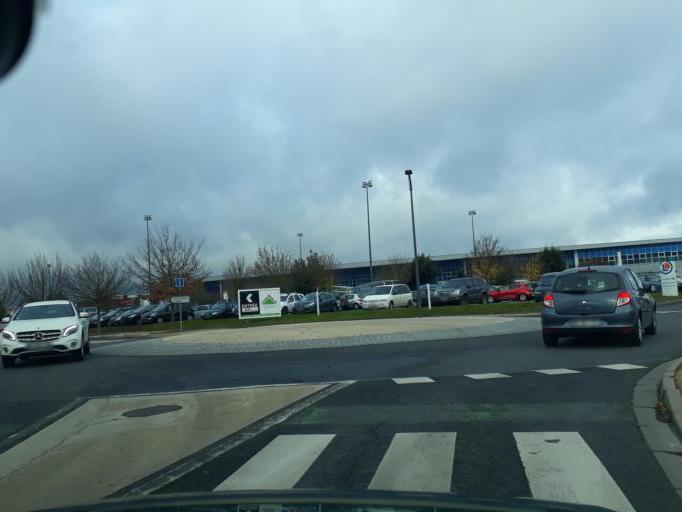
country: FR
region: Centre
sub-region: Departement du Loir-et-Cher
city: Villebarou
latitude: 47.6140
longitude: 1.3264
